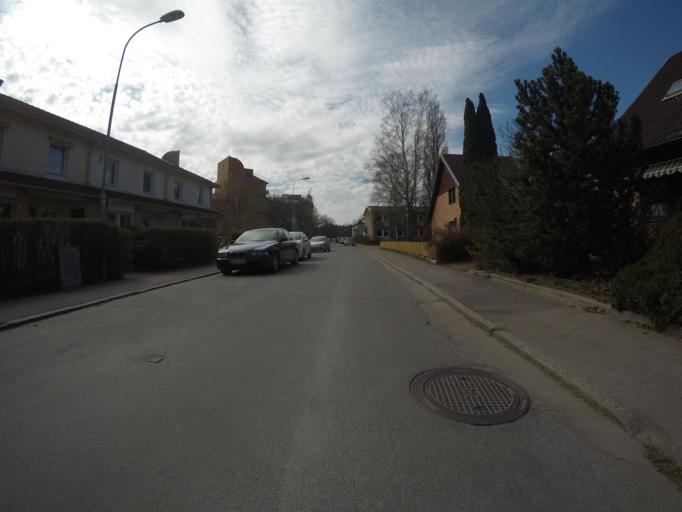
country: SE
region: Vaestmanland
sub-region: Vasteras
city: Vasteras
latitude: 59.6182
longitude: 16.5479
